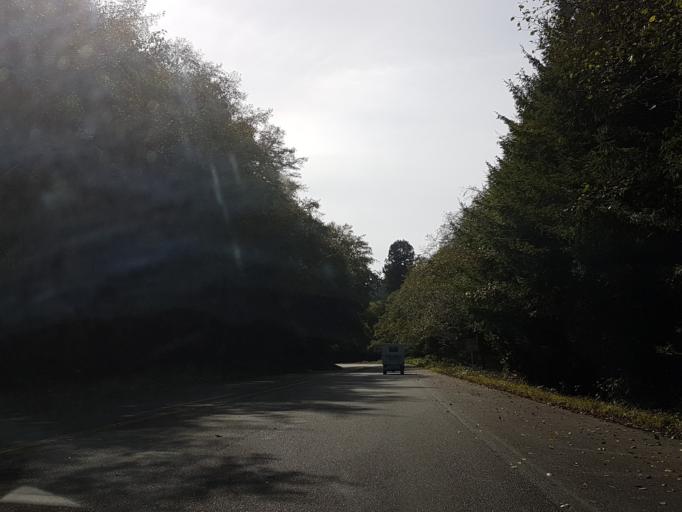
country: US
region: California
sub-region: Del Norte County
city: Bertsch-Oceanview
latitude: 41.4630
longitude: -124.0446
